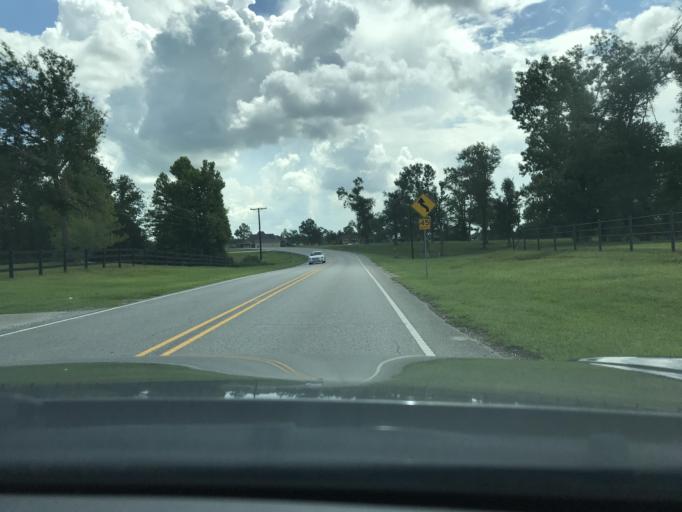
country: US
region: Louisiana
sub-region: Calcasieu Parish
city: Moss Bluff
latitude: 30.3398
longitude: -93.2469
